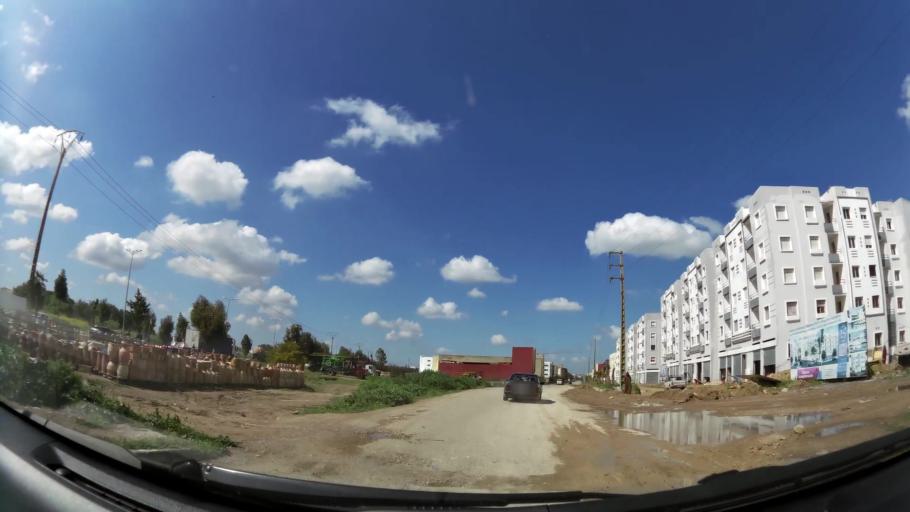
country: MA
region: Grand Casablanca
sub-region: Mediouna
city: Mediouna
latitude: 33.4429
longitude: -7.5201
